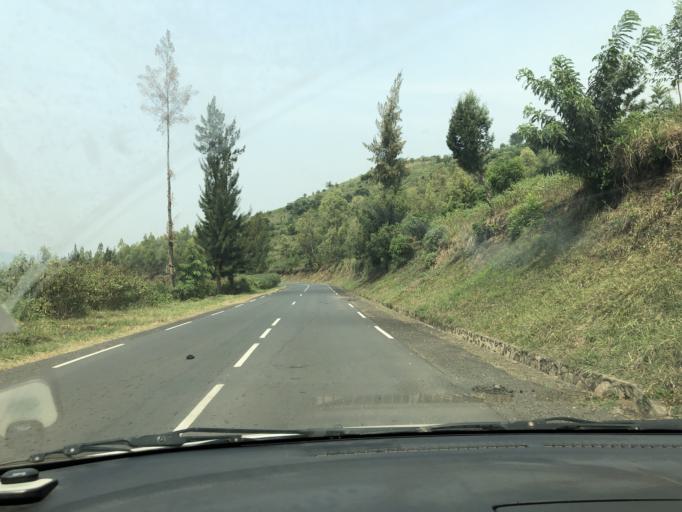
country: RW
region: Western Province
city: Cyangugu
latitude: -2.6683
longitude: 29.0018
